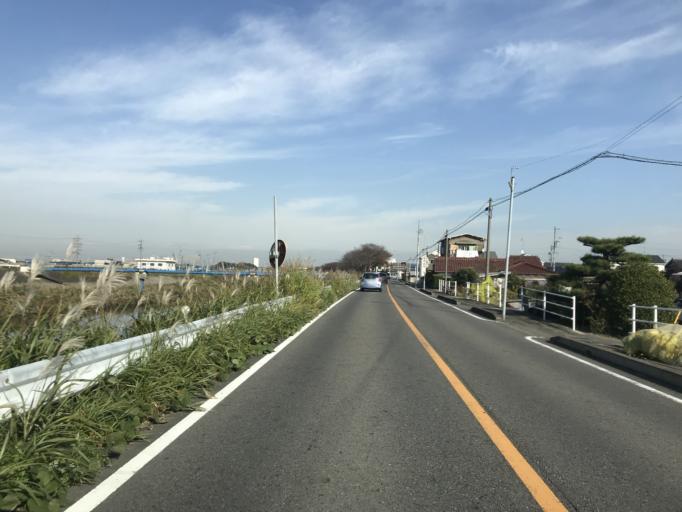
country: JP
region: Aichi
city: Iwakura
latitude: 35.2232
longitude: 136.8459
